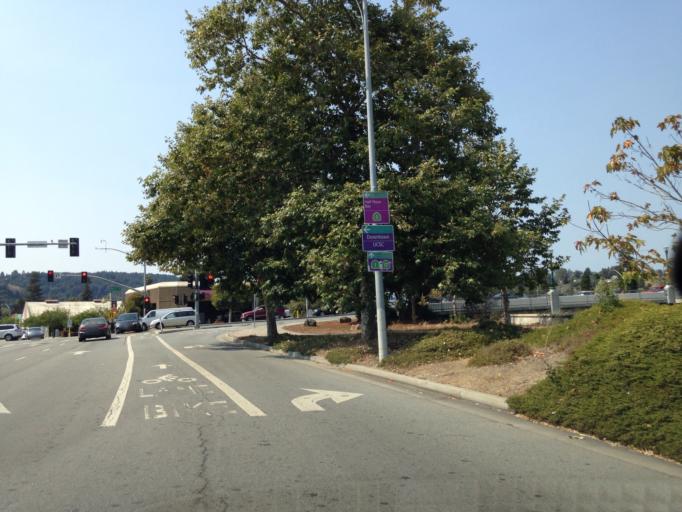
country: US
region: California
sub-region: Santa Cruz County
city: Santa Cruz
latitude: 36.9774
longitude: -122.0247
